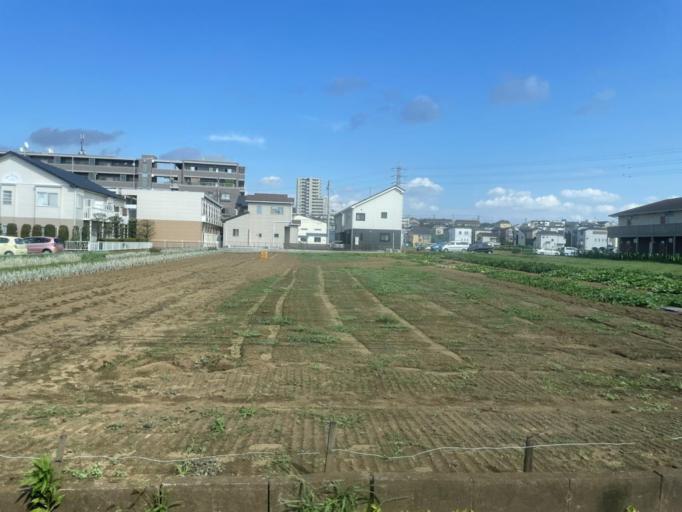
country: JP
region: Saitama
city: Asaka
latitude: 35.7997
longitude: 139.5850
